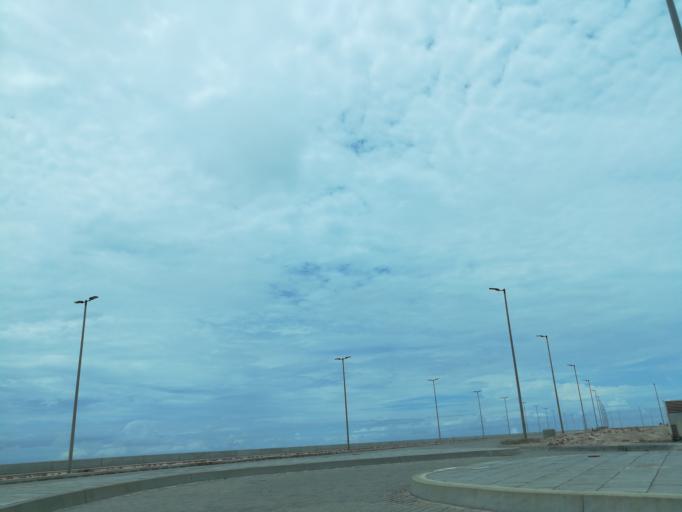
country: NG
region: Lagos
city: Ikoyi
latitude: 6.4052
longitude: 3.4174
